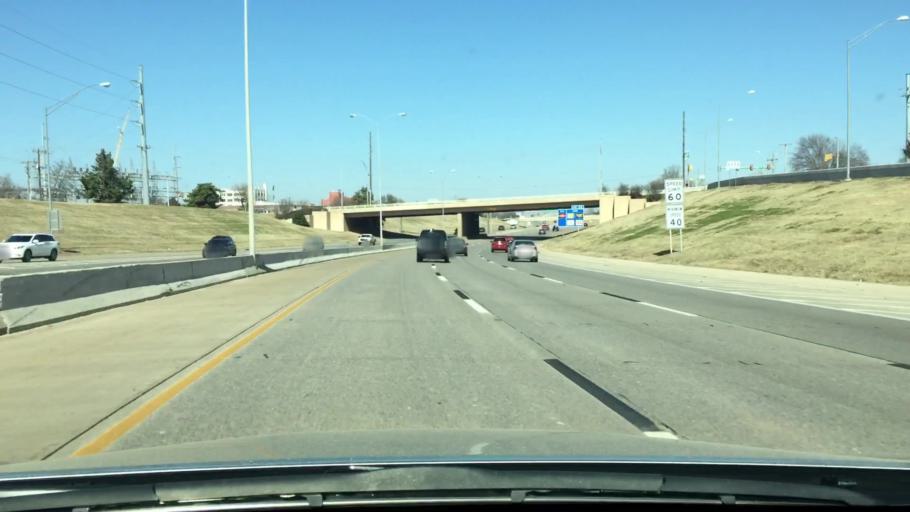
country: US
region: Oklahoma
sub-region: Oklahoma County
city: Oklahoma City
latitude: 35.4763
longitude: -97.5090
